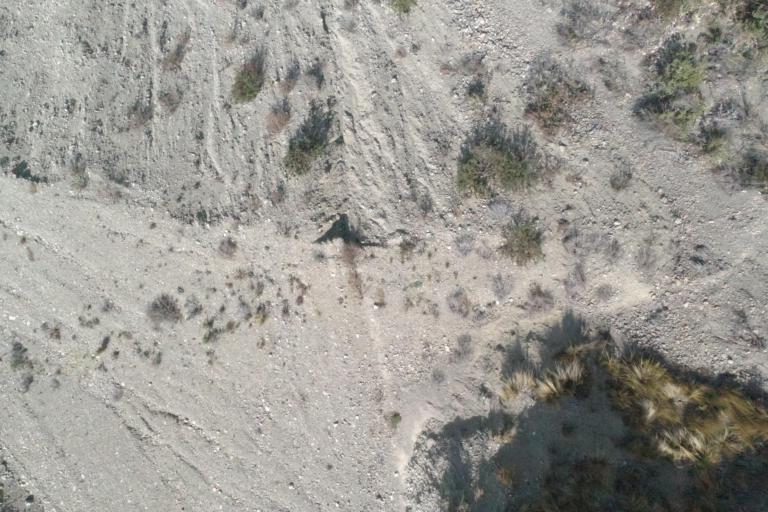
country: BO
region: La Paz
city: La Paz
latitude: -16.4745
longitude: -68.1005
